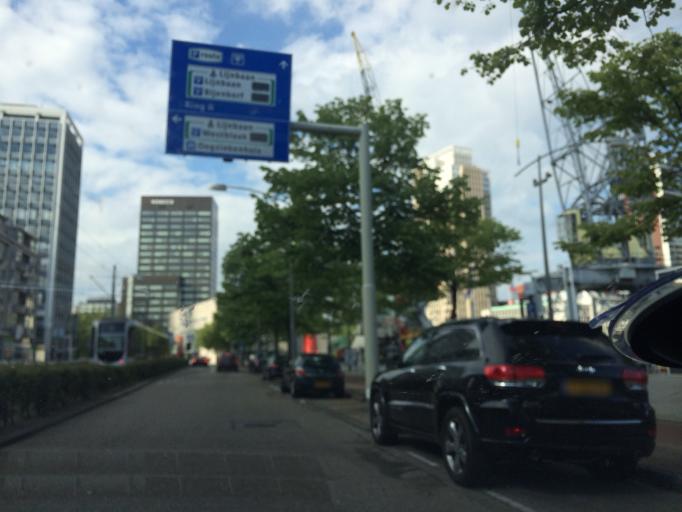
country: NL
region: South Holland
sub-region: Gemeente Rotterdam
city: Rotterdam
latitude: 51.9153
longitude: 4.4818
